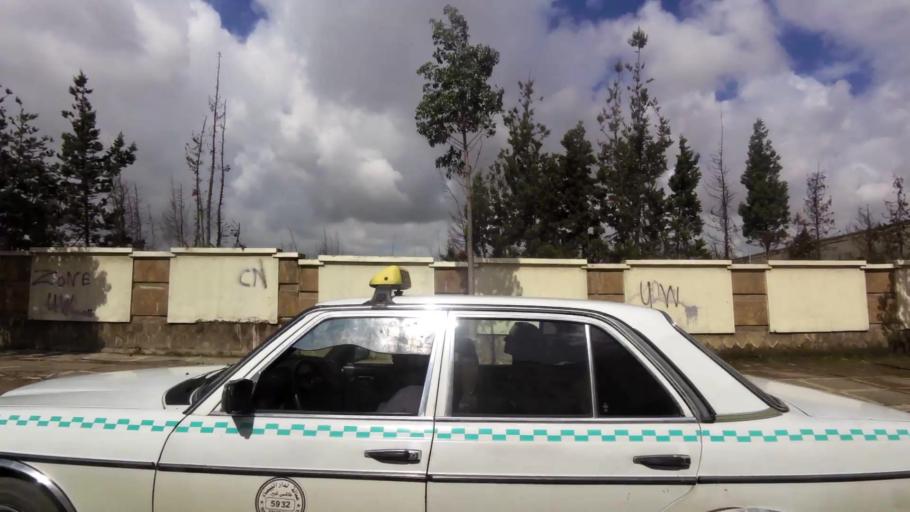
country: MA
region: Grand Casablanca
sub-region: Nouaceur
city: Bouskoura
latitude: 33.5199
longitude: -7.6525
